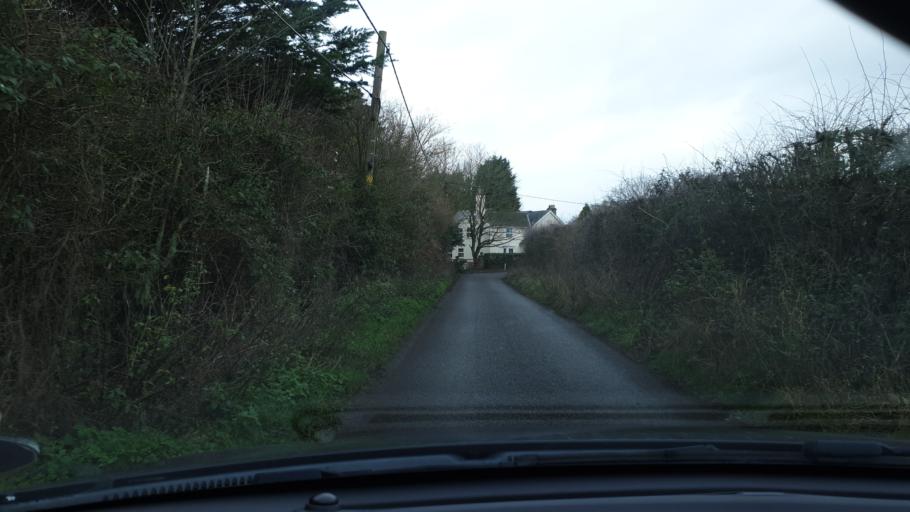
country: GB
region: England
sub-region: Essex
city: Alresford
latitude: 51.8576
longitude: 0.9924
